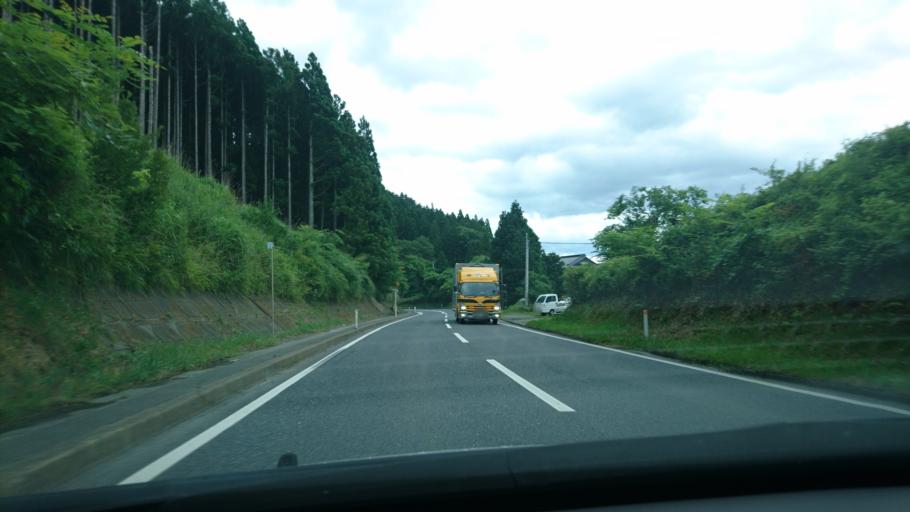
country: JP
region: Iwate
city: Kamaishi
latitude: 39.2090
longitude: 141.8695
